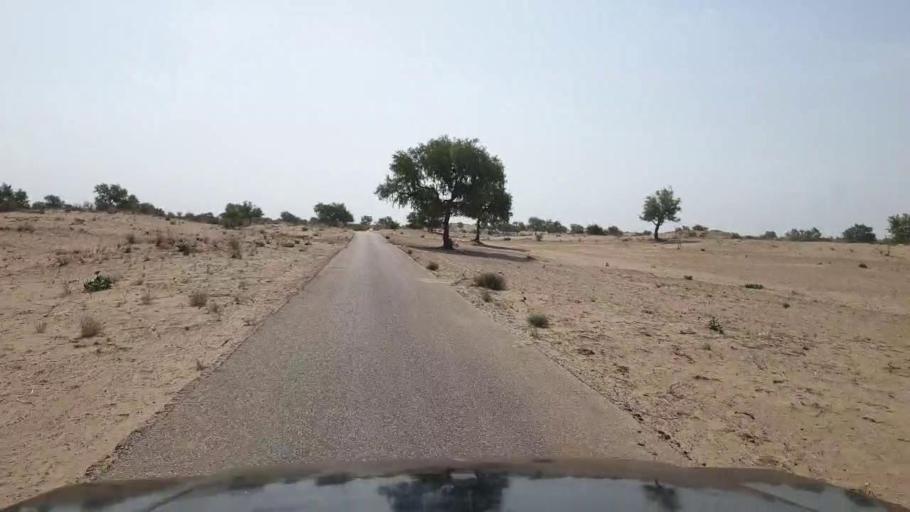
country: PK
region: Sindh
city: Islamkot
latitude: 24.9215
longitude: 70.1364
